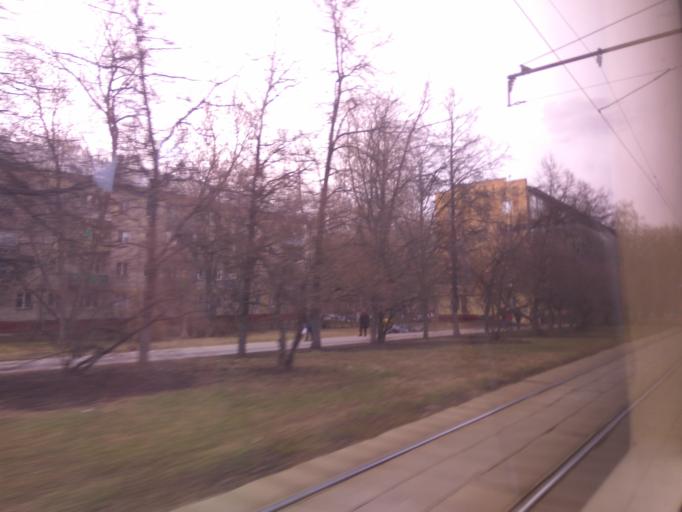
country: RU
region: Moscow
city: Leonovo
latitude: 55.8657
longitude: 37.6622
